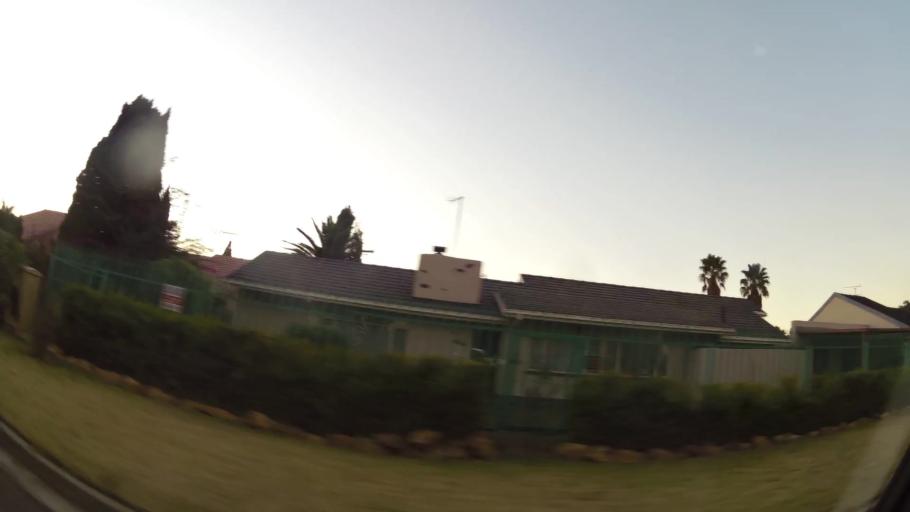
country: ZA
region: Gauteng
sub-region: Ekurhuleni Metropolitan Municipality
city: Germiston
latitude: -26.2625
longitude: 28.1573
